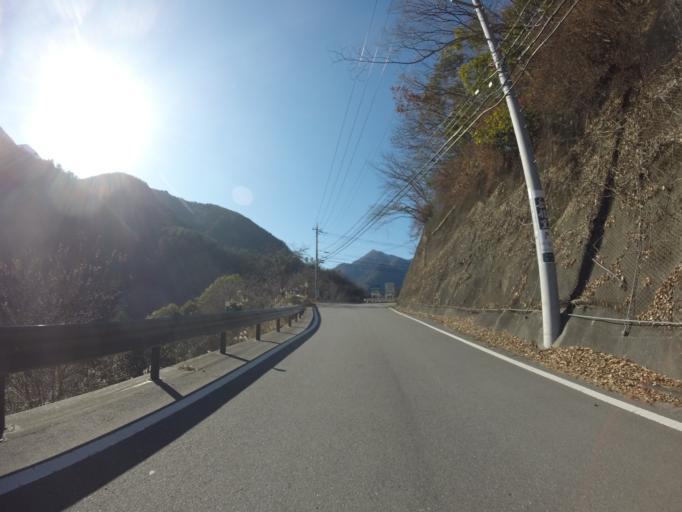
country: JP
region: Yamanashi
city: Ryuo
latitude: 35.4141
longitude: 138.3477
